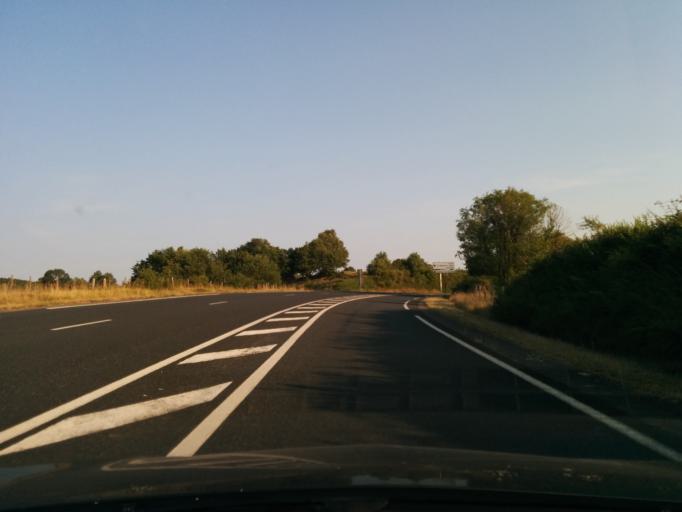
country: FR
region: Midi-Pyrenees
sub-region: Departement du Lot
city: Pradines
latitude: 44.5948
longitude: 1.5156
